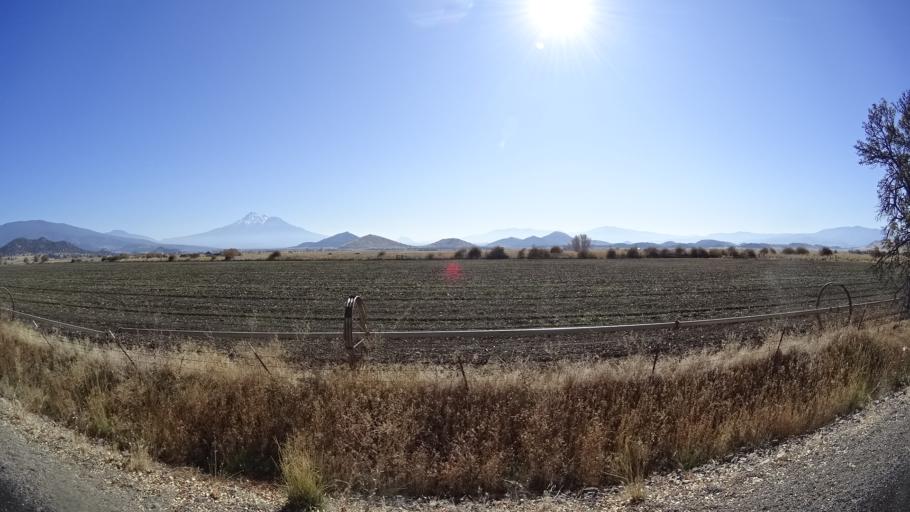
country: US
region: California
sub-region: Siskiyou County
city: Montague
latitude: 41.7263
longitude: -122.4062
